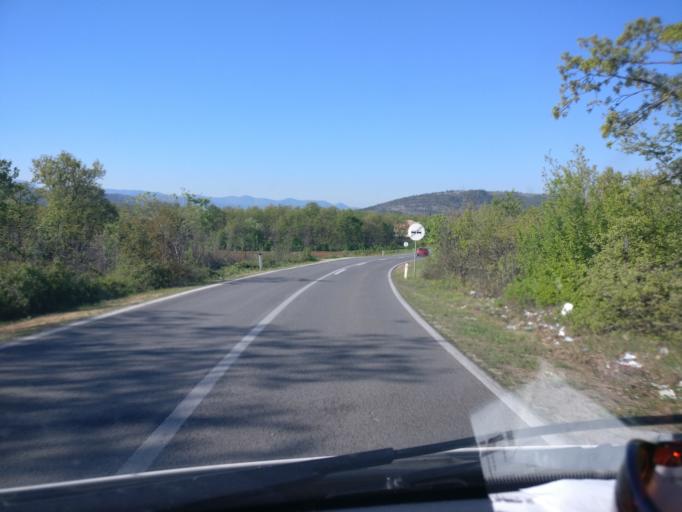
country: BA
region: Federation of Bosnia and Herzegovina
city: Tasovcici
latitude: 43.1288
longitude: 17.7647
